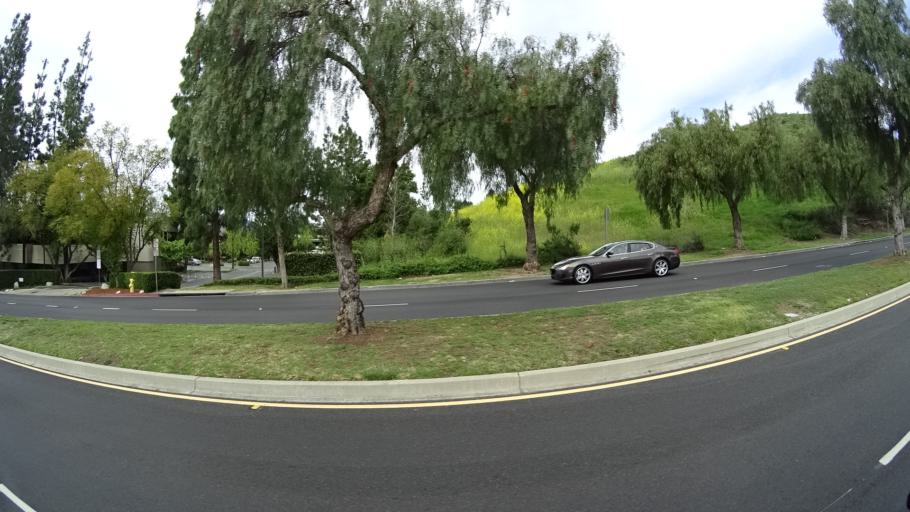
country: US
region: California
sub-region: Los Angeles County
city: Westlake Village
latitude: 34.1598
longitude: -118.8177
